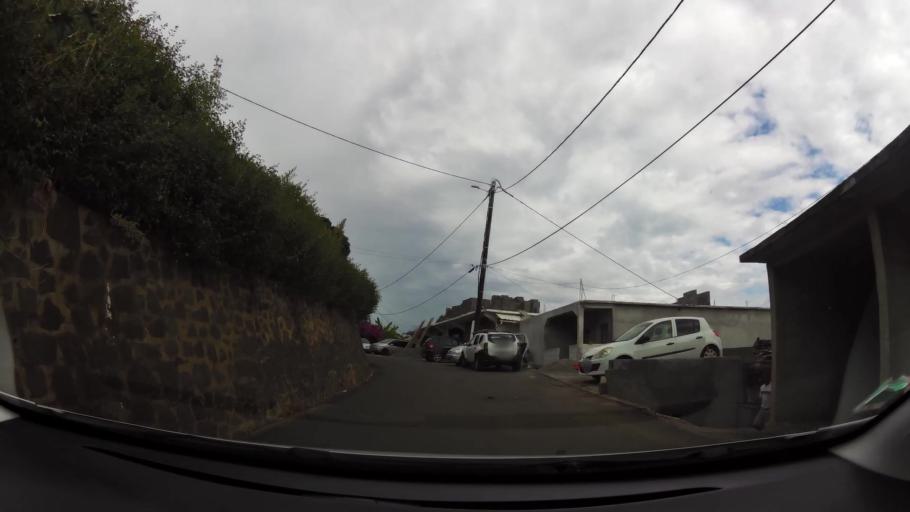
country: YT
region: Sada
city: Sada
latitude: -12.8525
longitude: 45.0956
